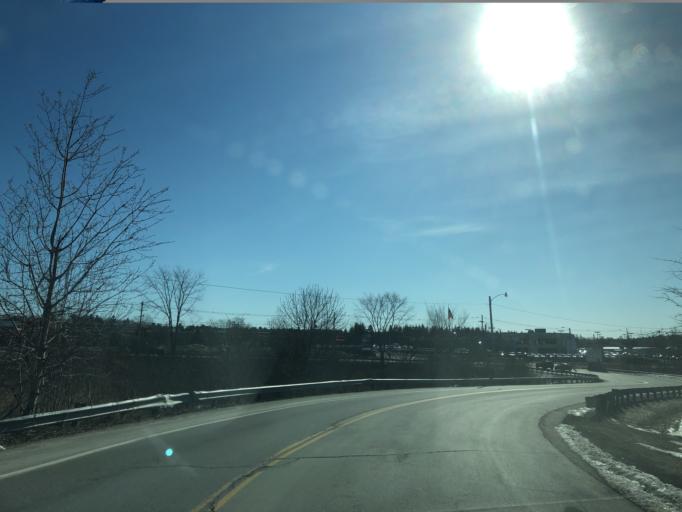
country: US
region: Maine
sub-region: Penobscot County
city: Brewer
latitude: 44.8293
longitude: -68.7428
